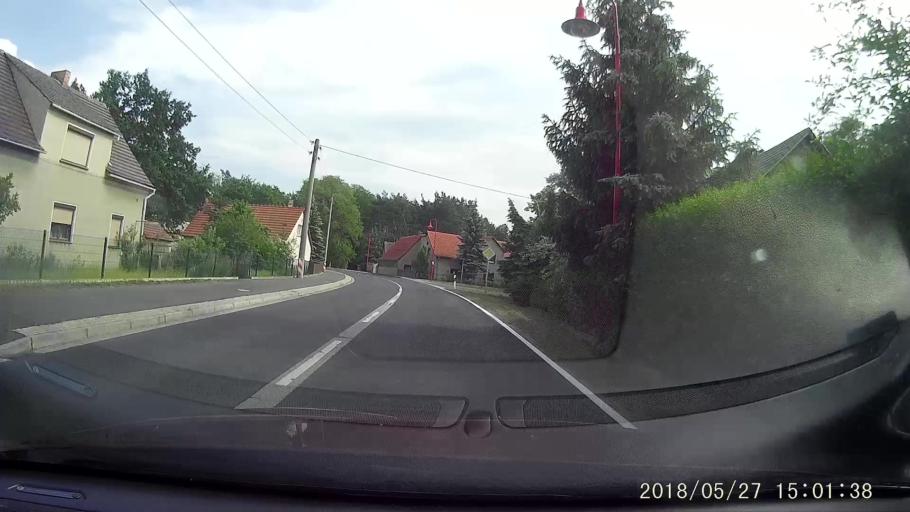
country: DE
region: Saxony
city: Mucka
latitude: 51.3306
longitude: 14.6906
